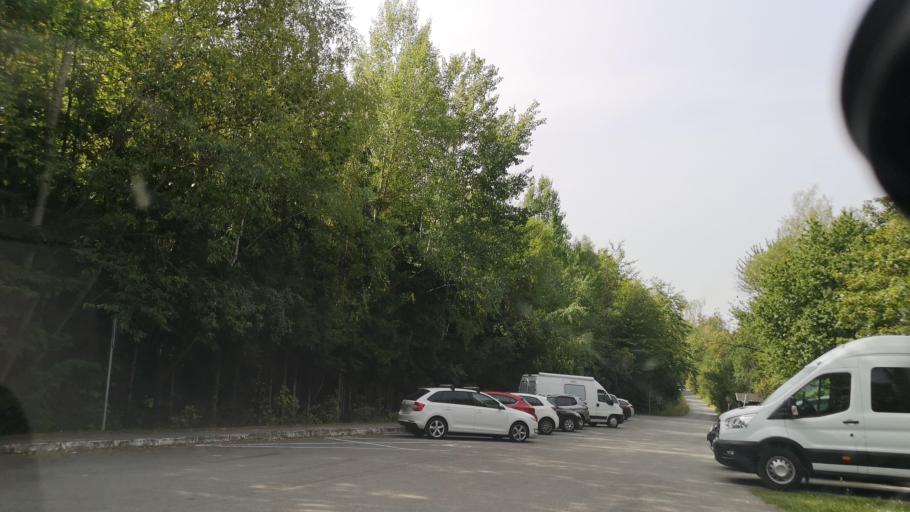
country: SK
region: Kosicky
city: Dobsina
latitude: 48.6636
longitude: 20.3052
